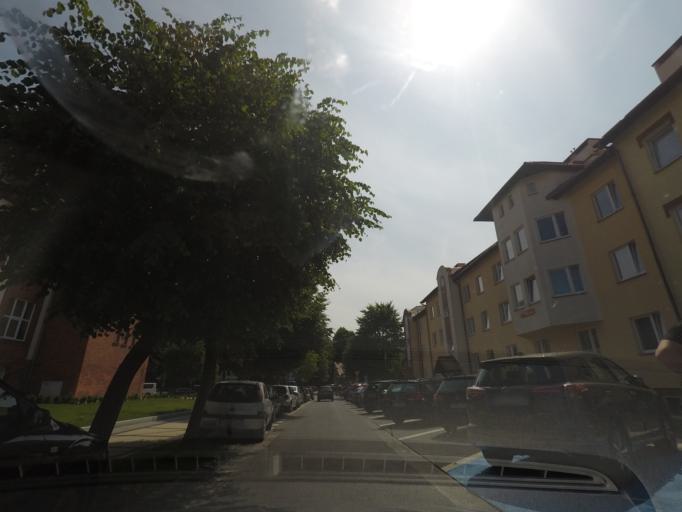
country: PL
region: Pomeranian Voivodeship
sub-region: Powiat slupski
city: Ustka
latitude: 54.5834
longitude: 16.8605
